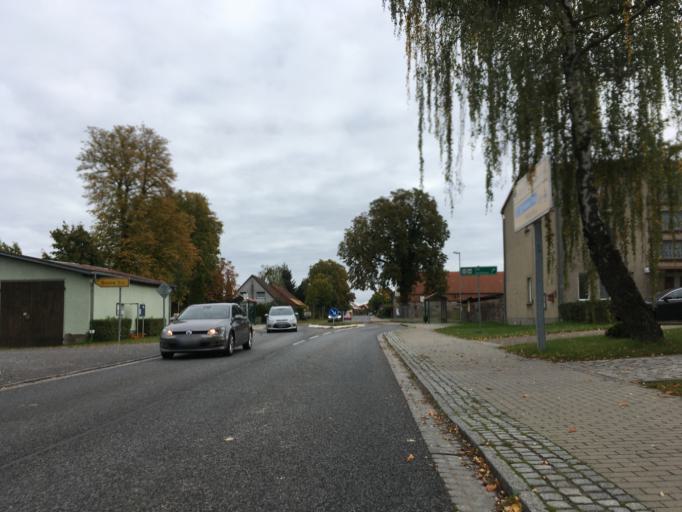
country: DE
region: Brandenburg
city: Werftpfuhl
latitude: 52.7033
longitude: 13.8859
